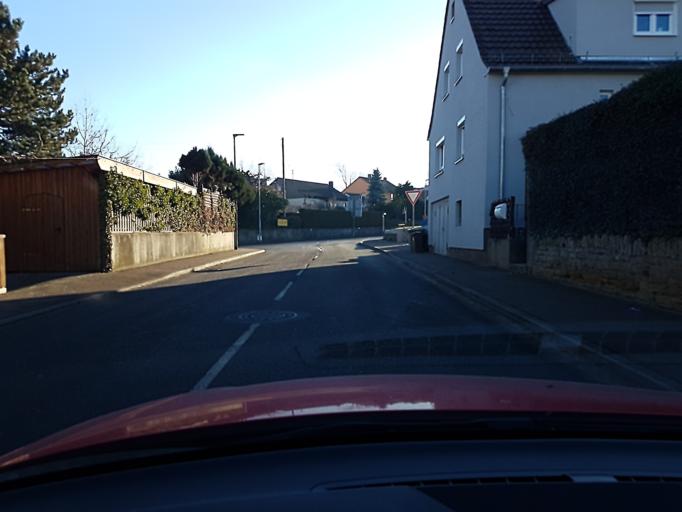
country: DE
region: Baden-Wuerttemberg
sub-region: Regierungsbezirk Stuttgart
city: Bonnigheim
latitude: 49.0373
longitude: 9.0910
